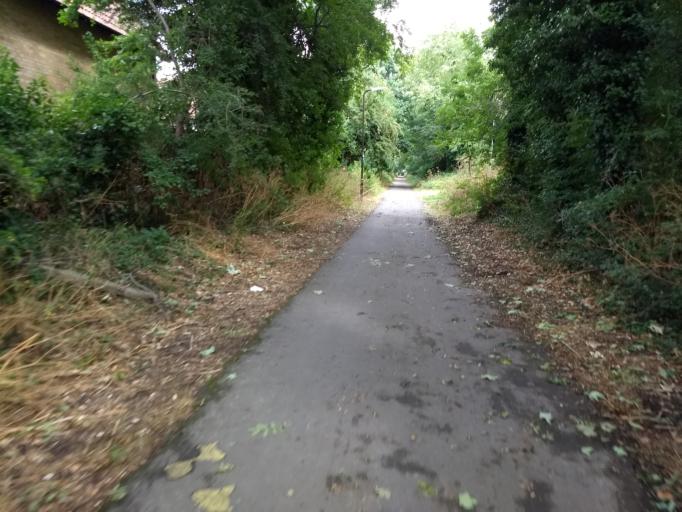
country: GB
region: England
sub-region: Milton Keynes
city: Bradwell
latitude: 52.0660
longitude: -0.7810
